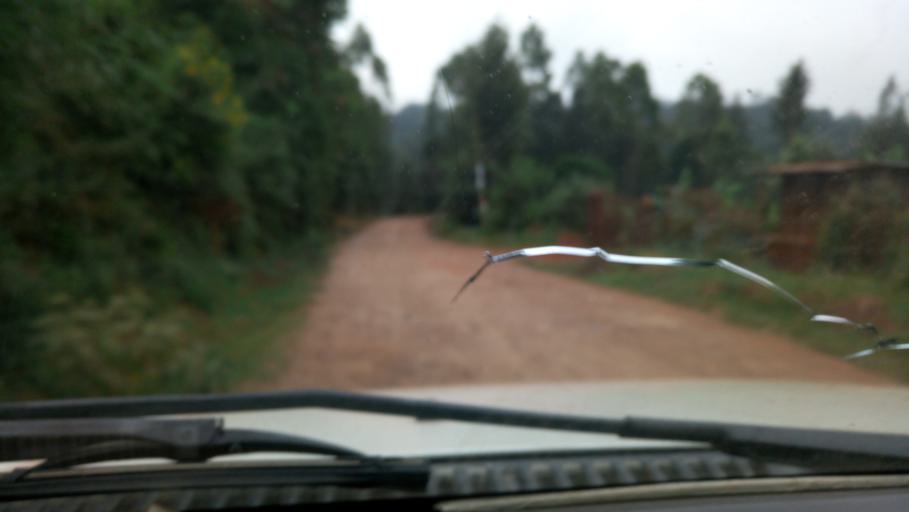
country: KE
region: Murang'a District
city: Kangema
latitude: -0.6807
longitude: 36.9800
